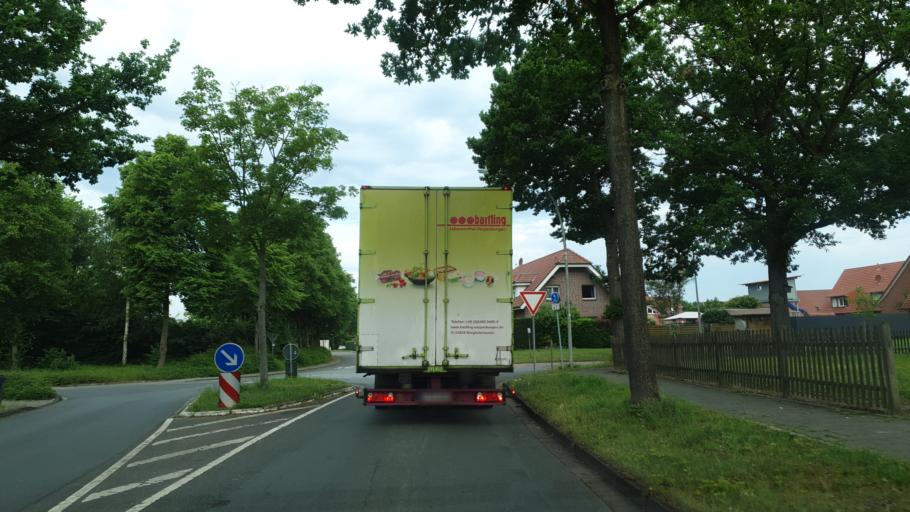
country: DE
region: North Rhine-Westphalia
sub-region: Regierungsbezirk Munster
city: Telgte
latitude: 52.0254
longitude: 7.7825
